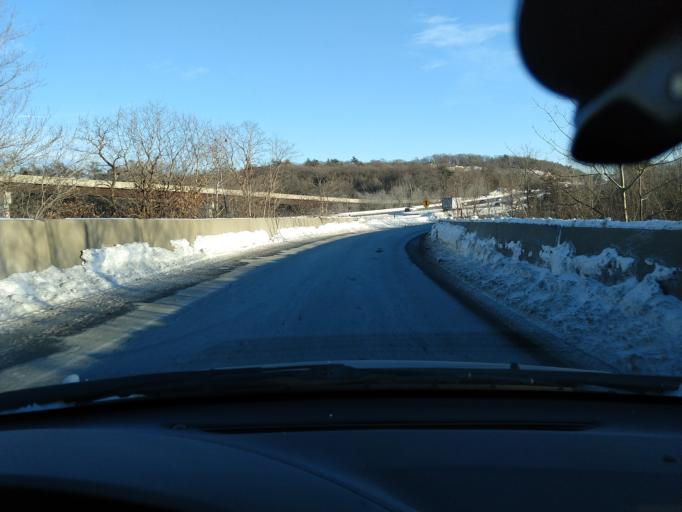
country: US
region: Massachusetts
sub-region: Middlesex County
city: Reading
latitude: 42.5196
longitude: -71.1338
